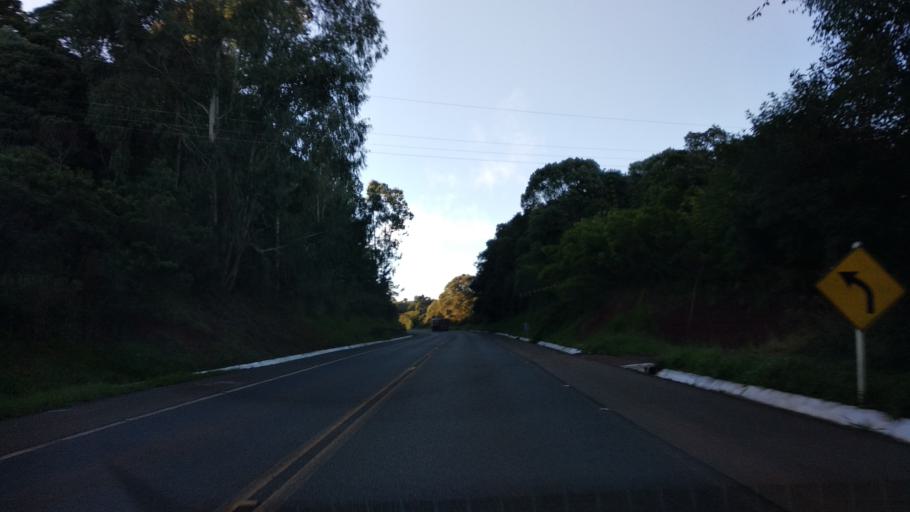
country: BR
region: Santa Catarina
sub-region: Correia Pinto
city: Correia Pinto
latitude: -27.6309
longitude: -50.6189
